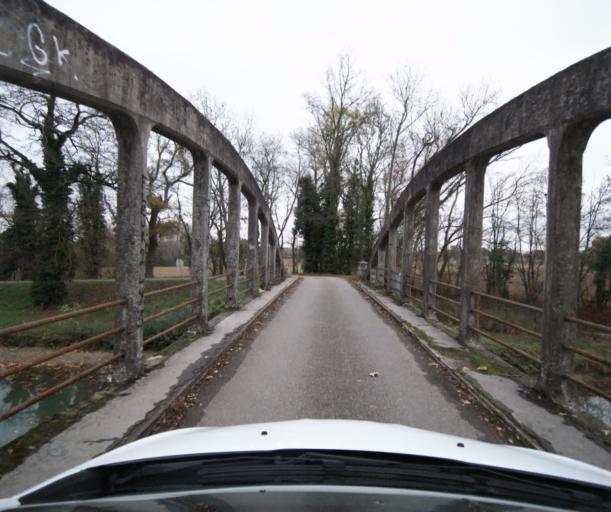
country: FR
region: Midi-Pyrenees
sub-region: Departement du Tarn-et-Garonne
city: Moissac
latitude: 44.0763
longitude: 1.0986
